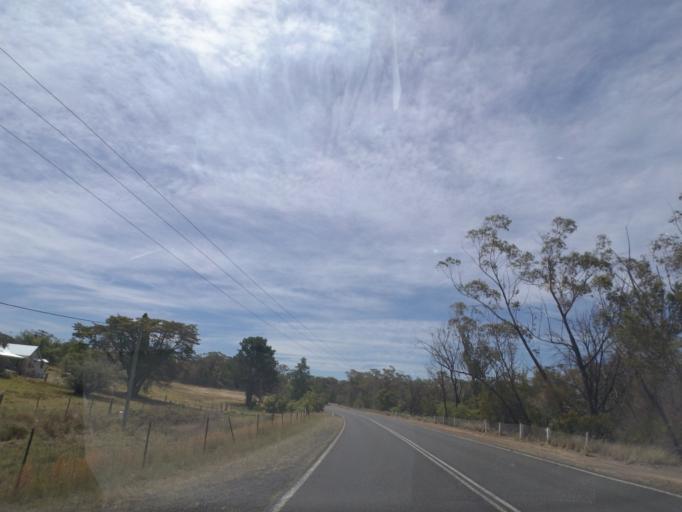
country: AU
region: New South Wales
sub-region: Wollondilly
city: Buxton
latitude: -34.3412
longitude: 150.5583
